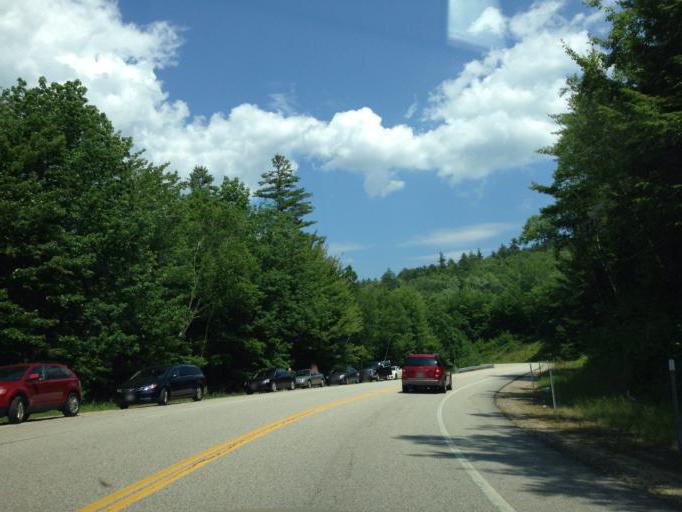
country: US
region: New Hampshire
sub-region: Carroll County
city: North Conway
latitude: 44.0129
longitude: -71.2618
